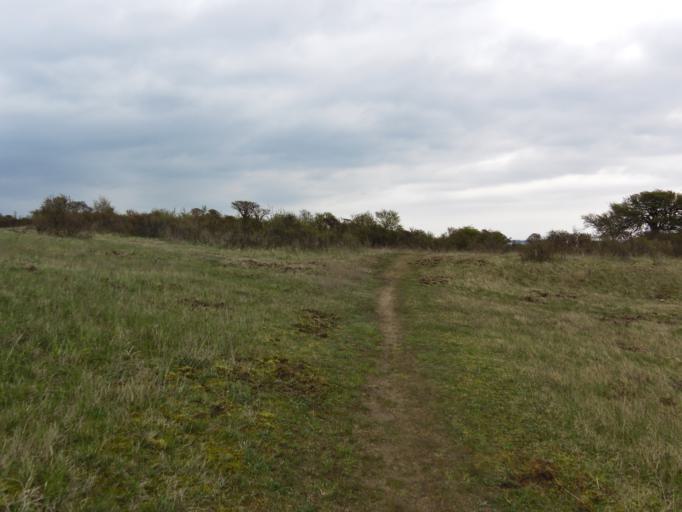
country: DE
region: Mecklenburg-Vorpommern
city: Hiddensee
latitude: 54.6019
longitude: 13.1328
